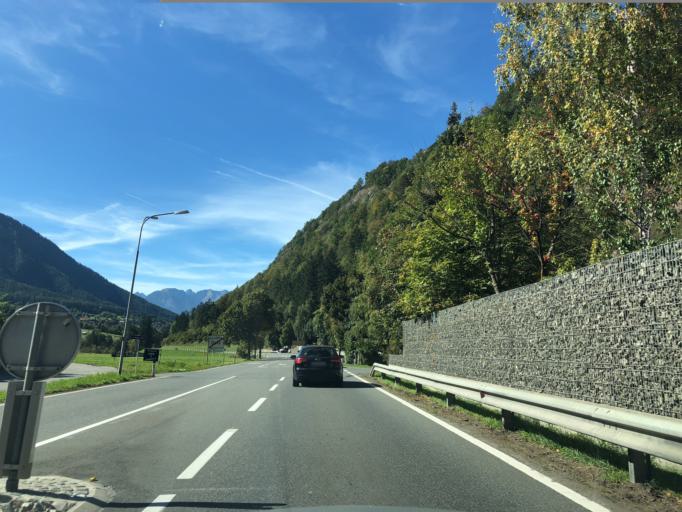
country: AT
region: Tyrol
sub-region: Politischer Bezirk Imst
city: Oetz
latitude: 47.2063
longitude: 10.8851
